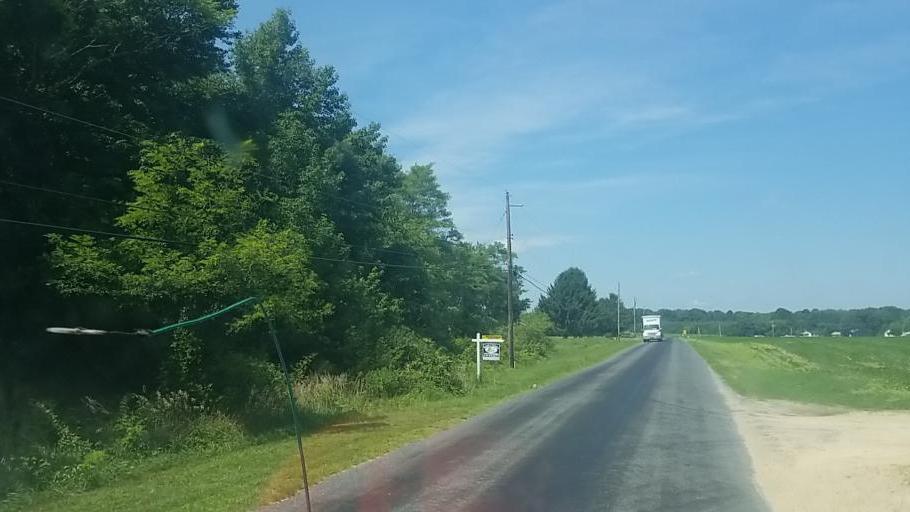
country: US
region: Maryland
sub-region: Caroline County
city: Denton
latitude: 38.8783
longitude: -75.7908
